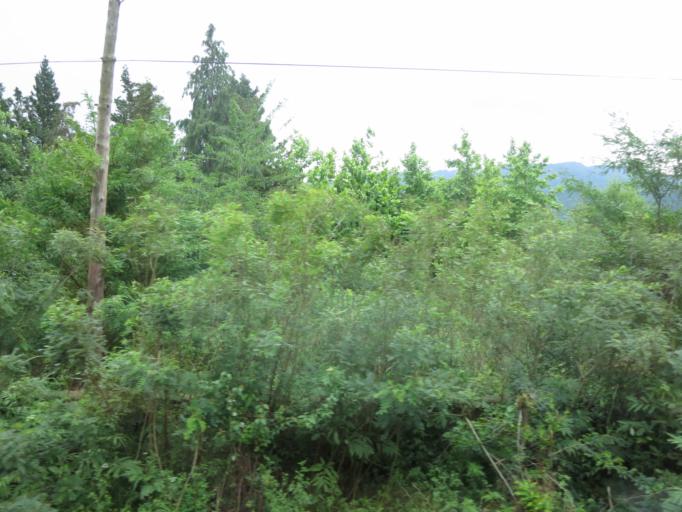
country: GE
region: Samegrelo and Zemo Svaneti
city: Abasha
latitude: 42.0961
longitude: 42.2340
